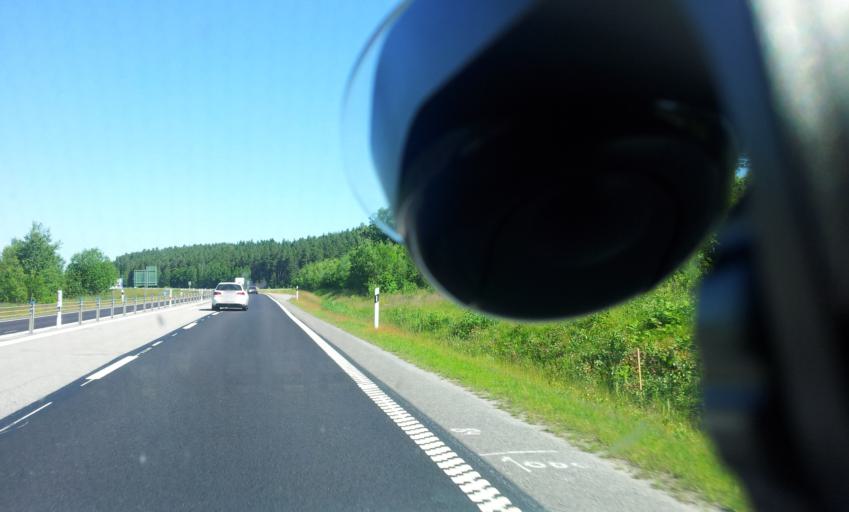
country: SE
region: OEstergoetland
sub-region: Soderkopings Kommun
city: Soederkoeping
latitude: 58.4978
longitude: 16.3025
